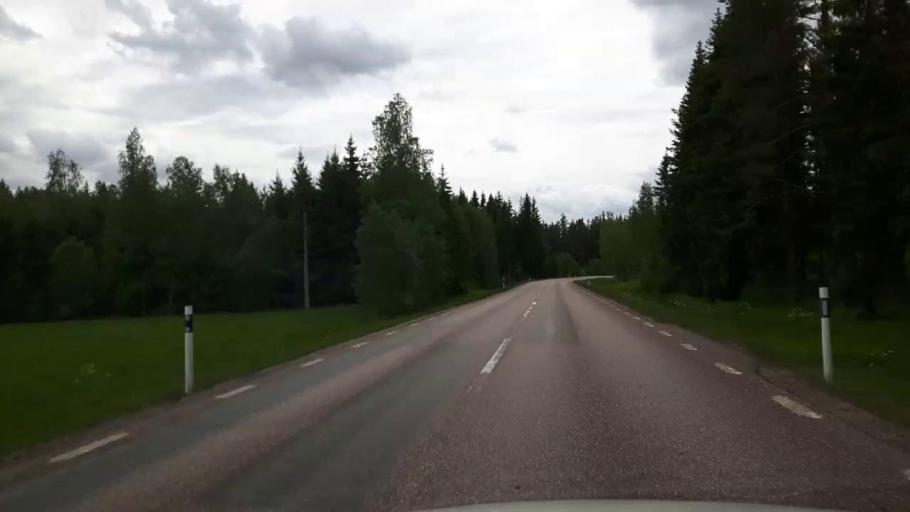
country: SE
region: Dalarna
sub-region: Hedemora Kommun
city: Brunna
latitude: 60.1700
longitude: 15.9968
